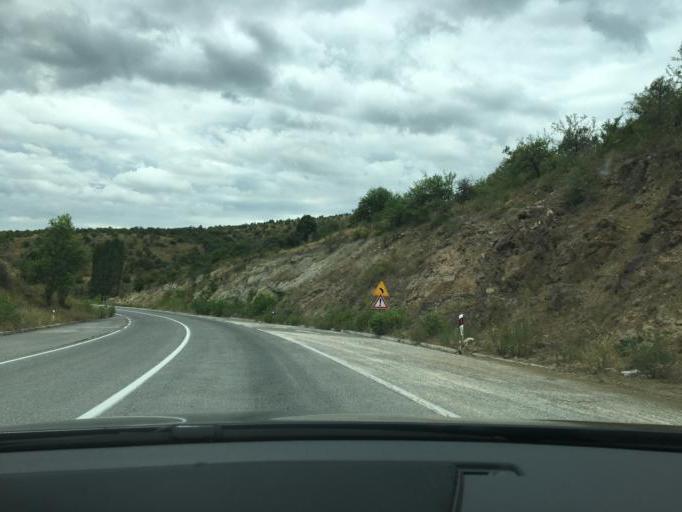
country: MK
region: Opstina Rankovce
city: Rankovce
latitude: 42.1488
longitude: 21.9995
